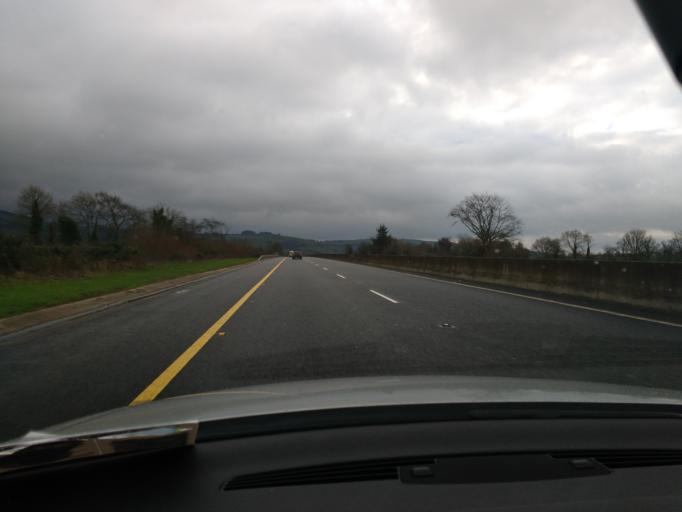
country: IE
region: Munster
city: Ballina
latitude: 52.8092
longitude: -8.3126
